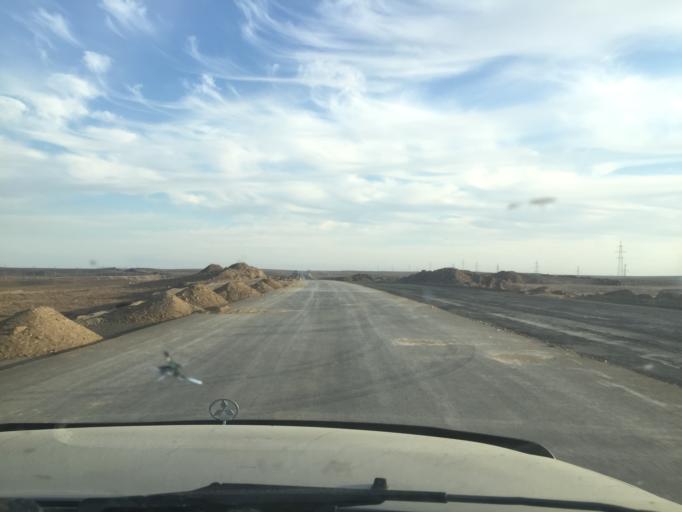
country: KZ
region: Zhambyl
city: Mynaral
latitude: 45.2800
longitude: 73.7789
